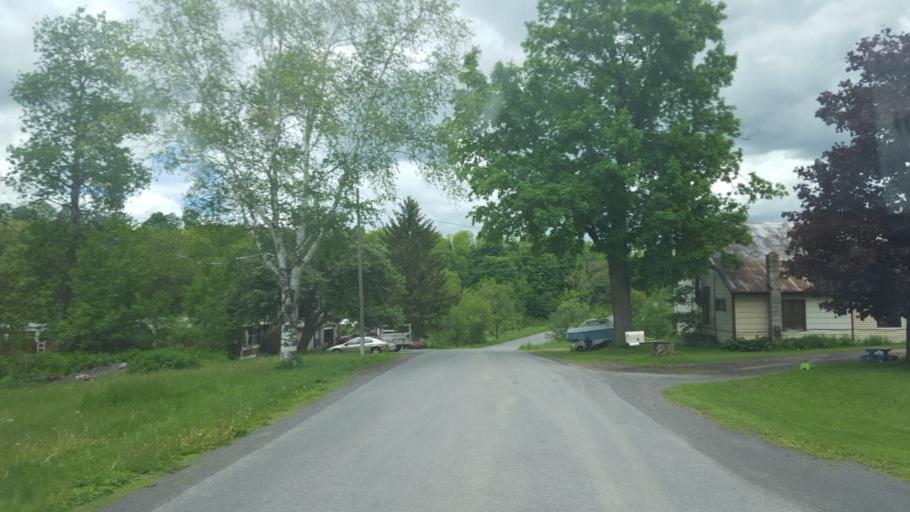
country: US
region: New York
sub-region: Otsego County
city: Richfield Springs
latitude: 42.8683
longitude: -75.0285
